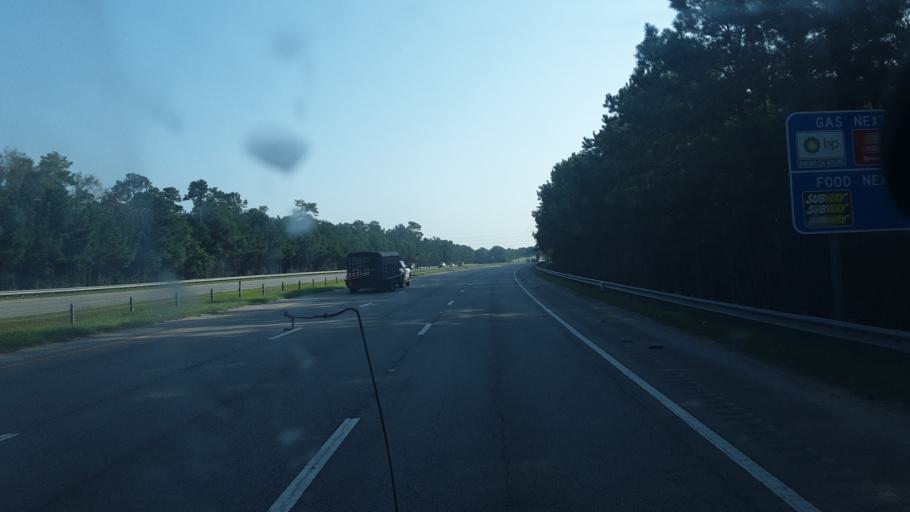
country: US
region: South Carolina
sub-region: Horry County
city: North Myrtle Beach
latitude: 33.8700
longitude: -78.6892
